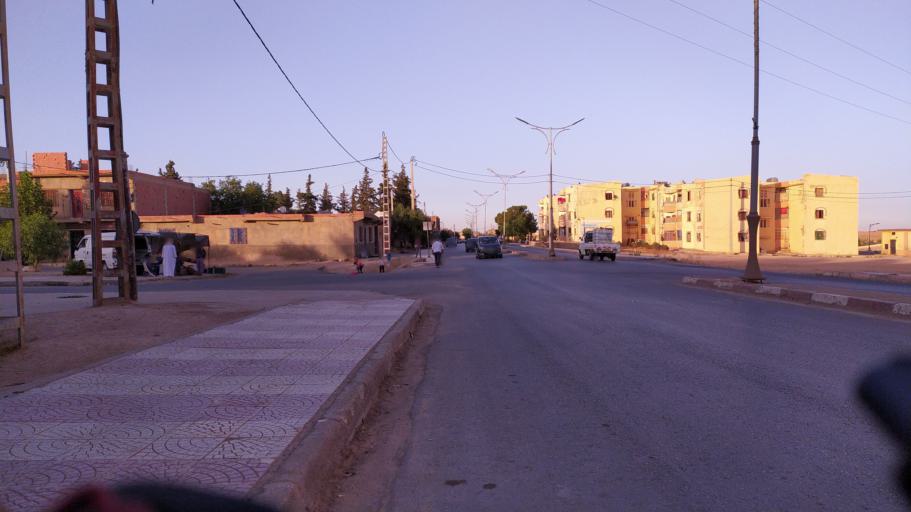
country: DZ
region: Tiaret
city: Frenda
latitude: 34.8886
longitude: 1.2419
